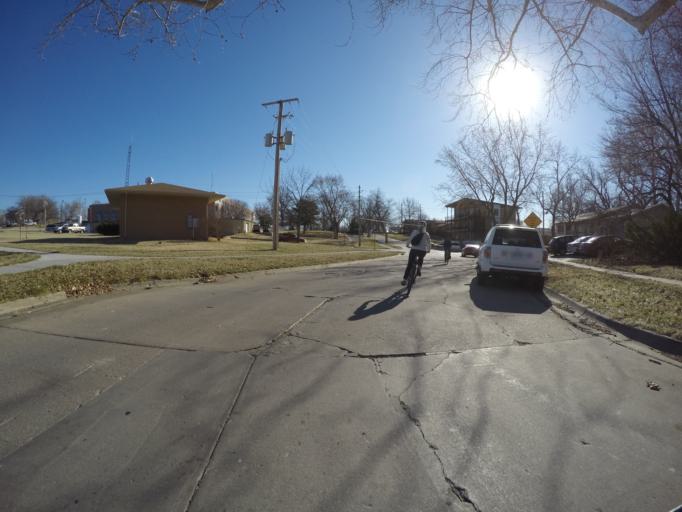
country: US
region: Kansas
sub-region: Riley County
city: Manhattan
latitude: 39.1912
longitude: -96.5917
